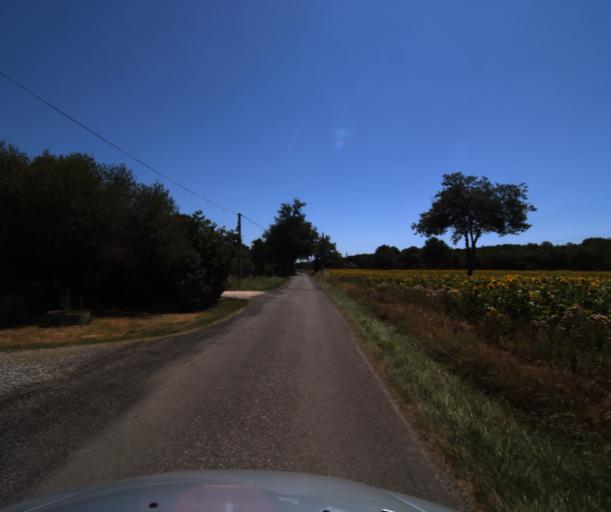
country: FR
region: Midi-Pyrenees
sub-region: Departement de la Haute-Garonne
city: Muret
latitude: 43.4534
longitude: 1.3491
